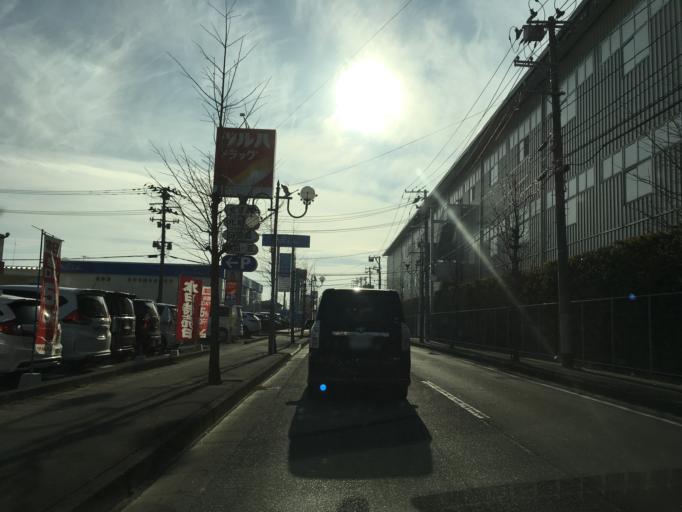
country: JP
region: Miyagi
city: Wakuya
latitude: 38.6885
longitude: 141.1885
